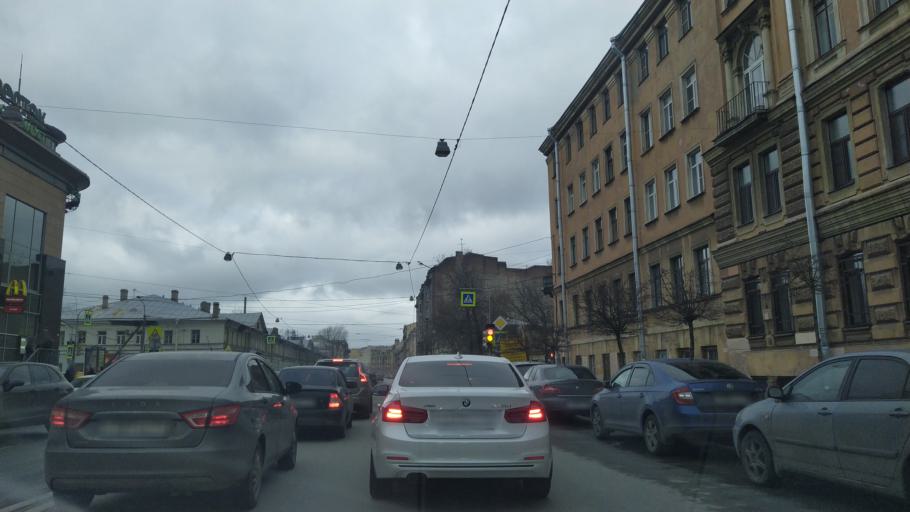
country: RU
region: St.-Petersburg
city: Centralniy
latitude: 59.9193
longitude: 30.3402
